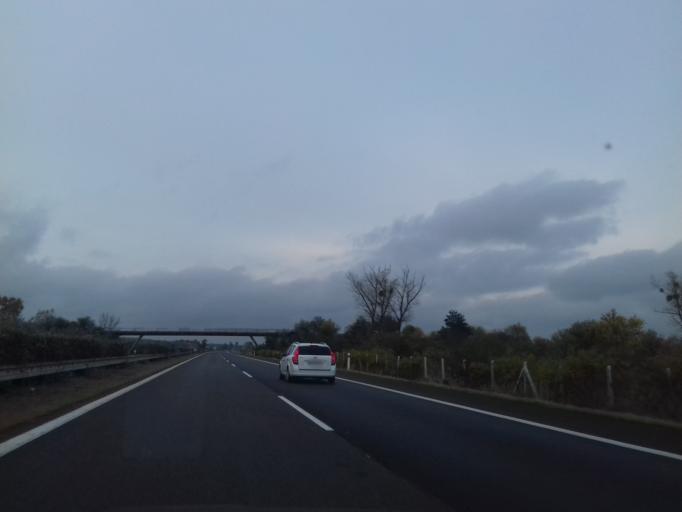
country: CZ
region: South Moravian
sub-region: Okres Breclav
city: Lanzhot
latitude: 48.6579
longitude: 16.9922
